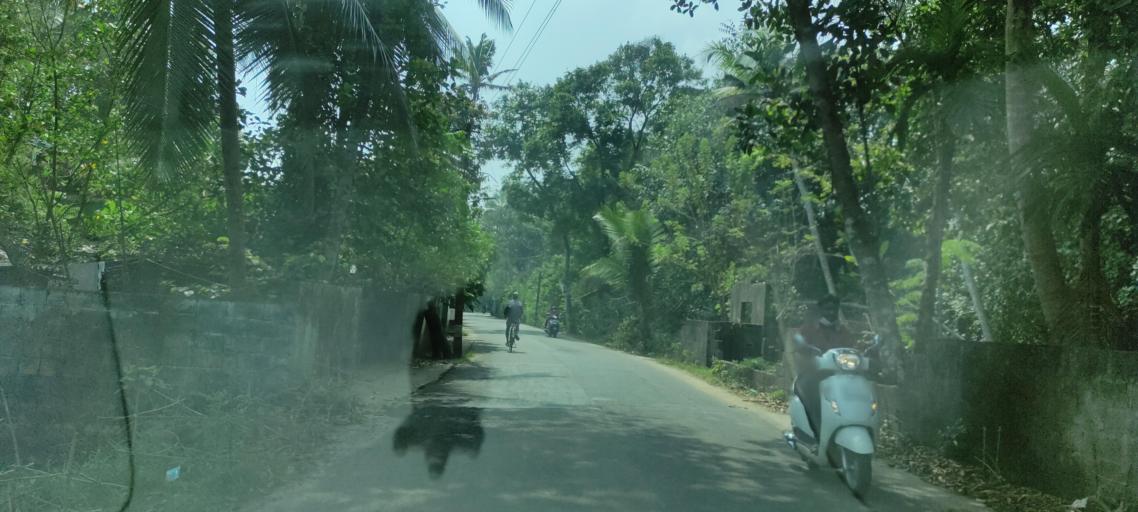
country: IN
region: Kerala
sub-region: Alappuzha
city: Shertallai
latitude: 9.6476
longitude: 76.3558
